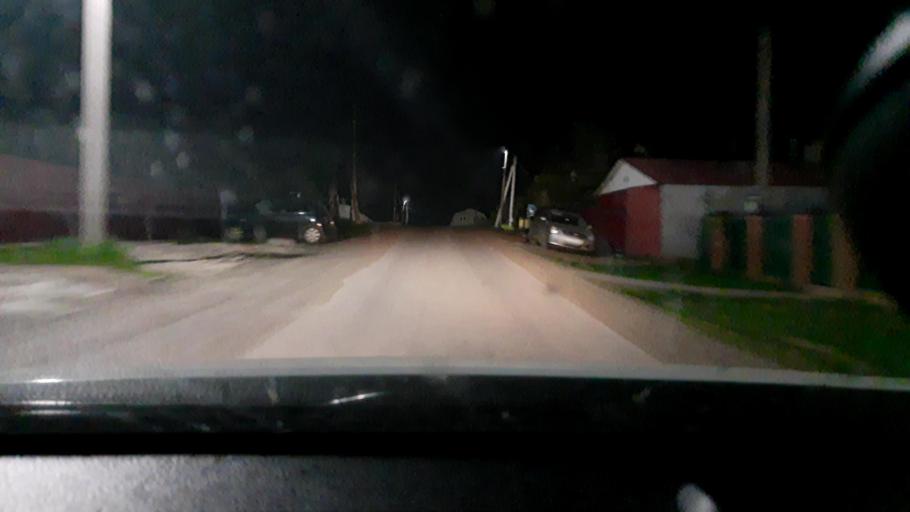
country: RU
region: Bashkortostan
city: Ufa
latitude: 54.5929
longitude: 55.9554
